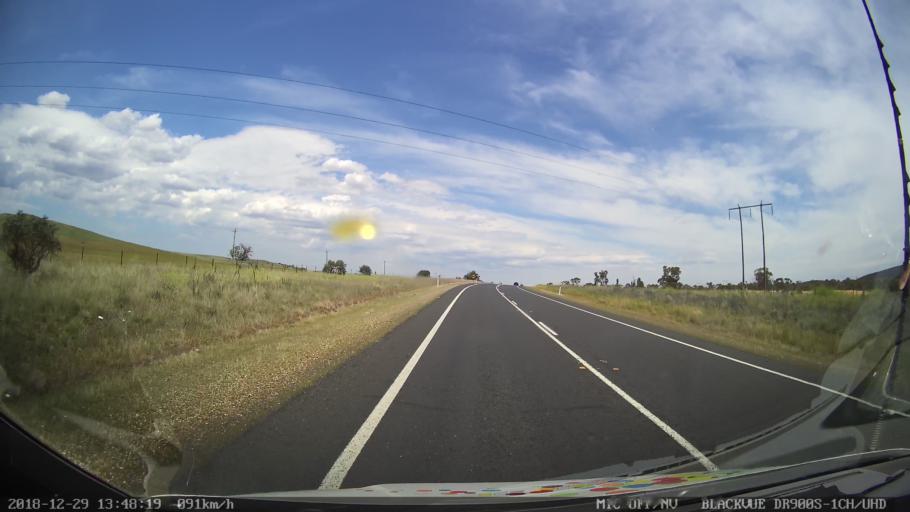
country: AU
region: New South Wales
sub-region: Cooma-Monaro
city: Cooma
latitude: -36.1385
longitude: 149.1473
